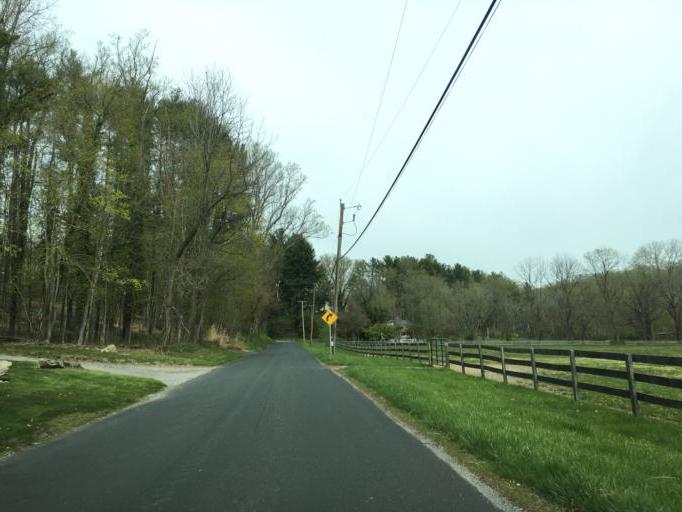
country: US
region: Maryland
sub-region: Baltimore County
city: Hunt Valley
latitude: 39.5684
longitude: -76.6166
